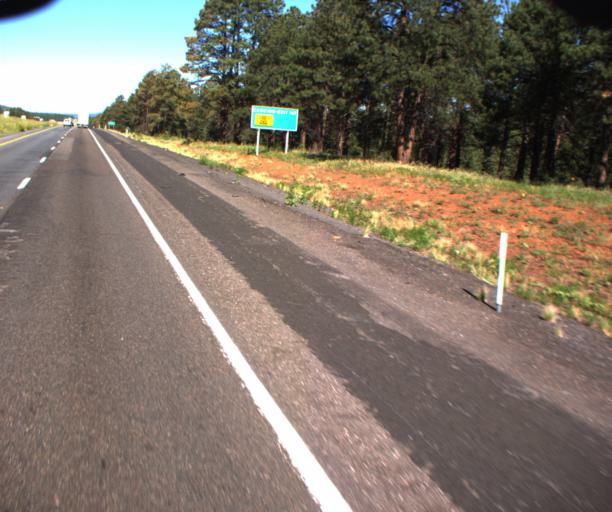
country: US
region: Arizona
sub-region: Coconino County
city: Williams
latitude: 35.2586
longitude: -112.1036
